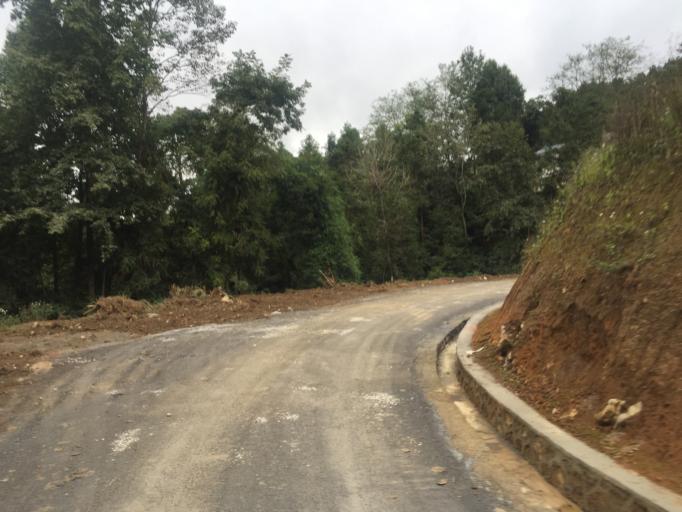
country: CN
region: Guizhou Sheng
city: Zhongba
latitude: 27.9794
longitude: 108.2224
